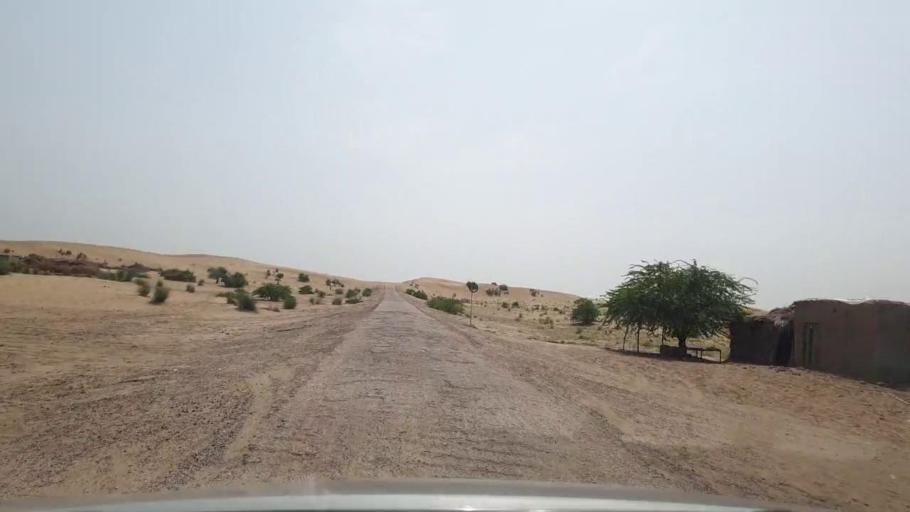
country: PK
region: Sindh
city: Rohri
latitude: 27.6179
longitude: 69.1145
